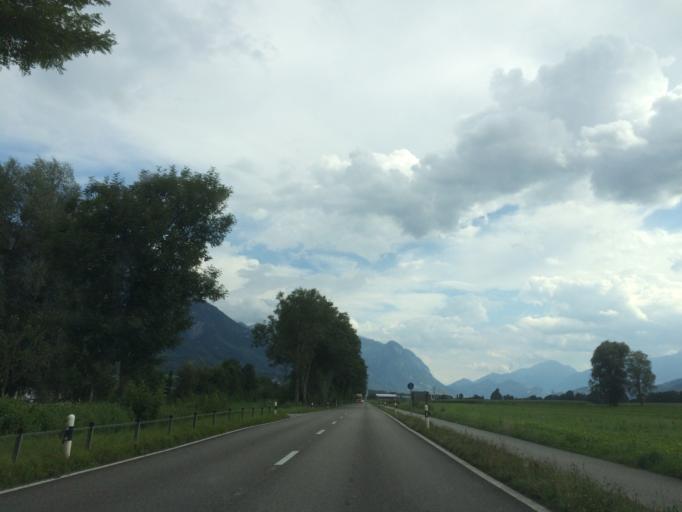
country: CH
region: Saint Gallen
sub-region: Wahlkreis Werdenberg
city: Haag (Rheintal)
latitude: 47.1917
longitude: 9.5037
